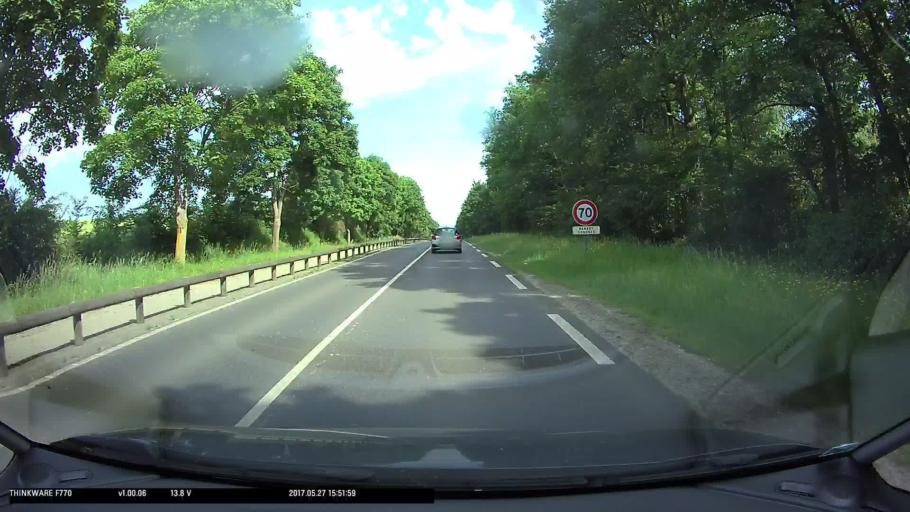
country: FR
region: Ile-de-France
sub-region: Departement du Val-d'Oise
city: Chars
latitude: 49.1532
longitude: 1.9583
